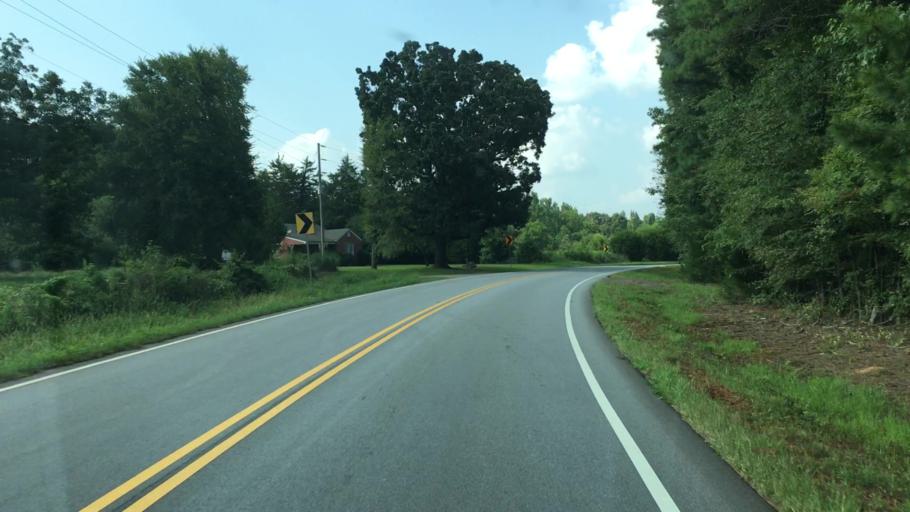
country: US
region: Georgia
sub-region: Jasper County
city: Monticello
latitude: 33.3967
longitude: -83.7596
